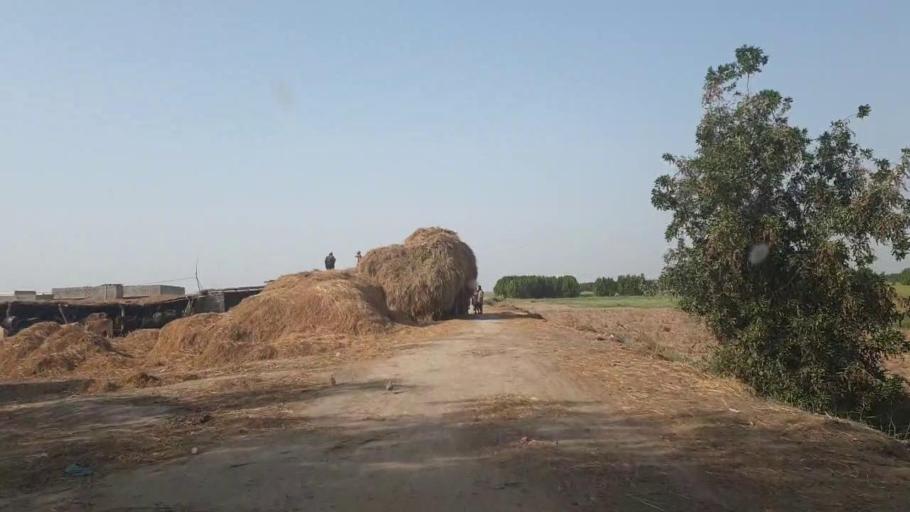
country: PK
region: Sindh
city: Kario
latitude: 24.5799
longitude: 68.5442
